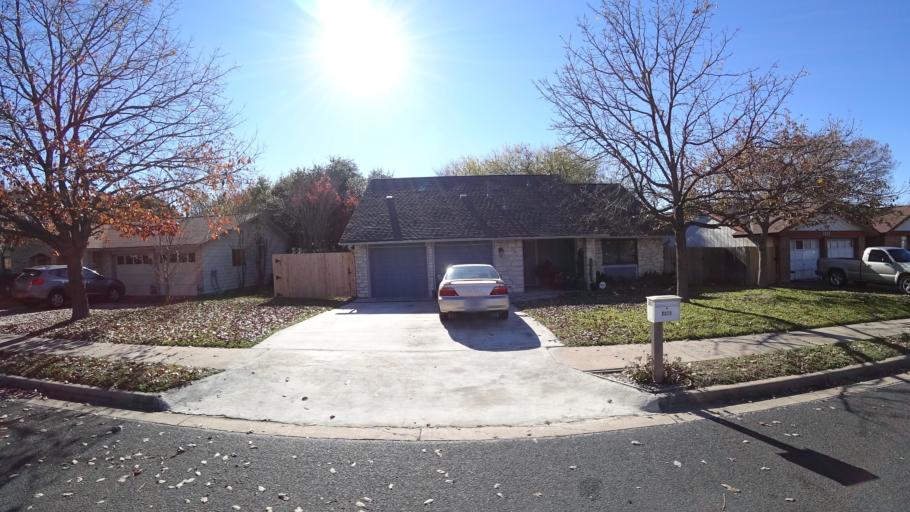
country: US
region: Texas
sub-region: Travis County
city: Wells Branch
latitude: 30.4204
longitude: -97.6922
